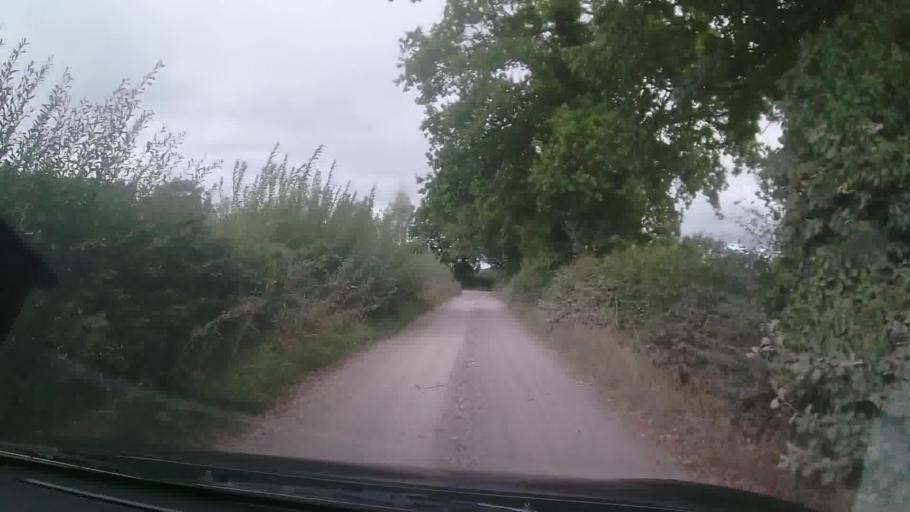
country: GB
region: England
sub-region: Shropshire
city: Prees
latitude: 52.8810
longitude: -2.6308
